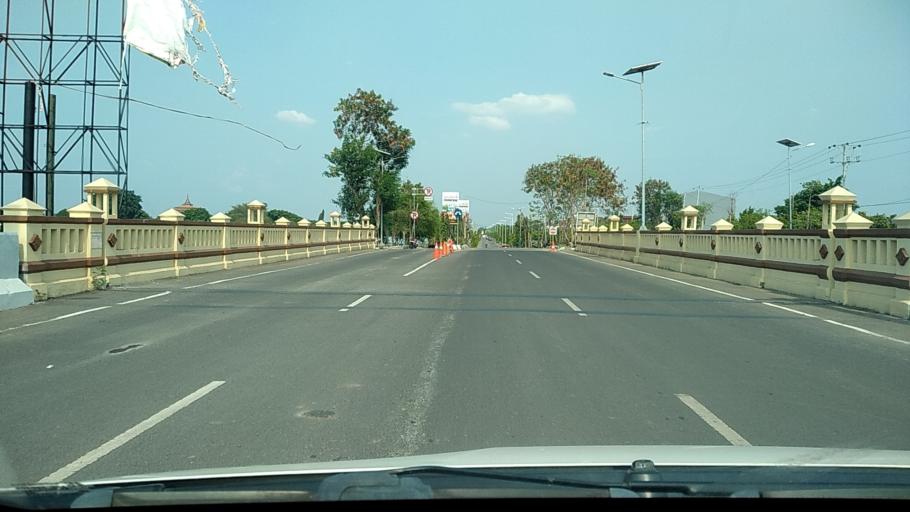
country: ID
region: Central Java
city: Semarang
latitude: -6.9632
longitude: 110.3831
